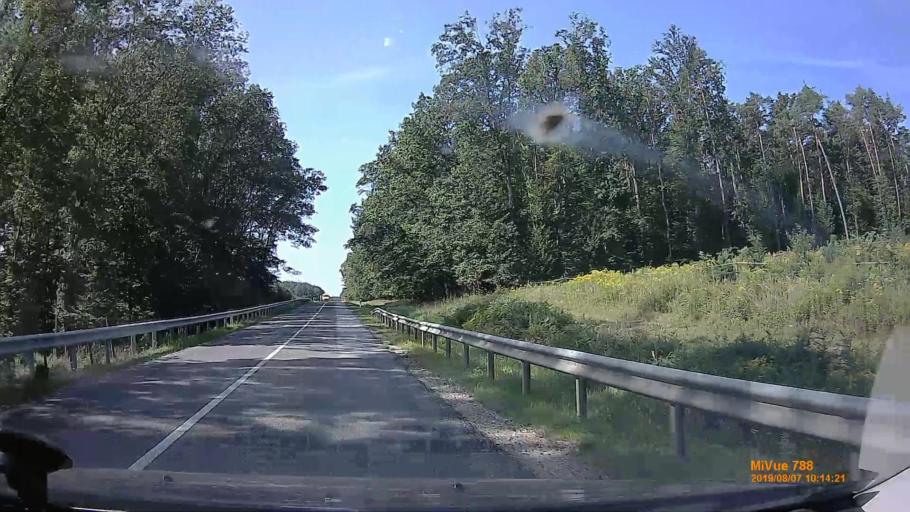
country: HU
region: Zala
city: Lenti
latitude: 46.6563
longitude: 16.6295
